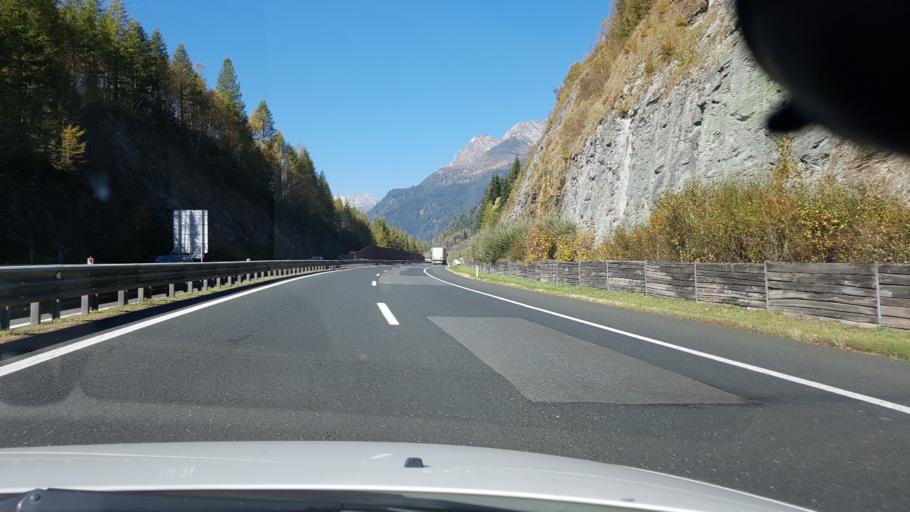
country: AT
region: Salzburg
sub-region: Politischer Bezirk Tamsweg
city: Zederhaus
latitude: 47.1426
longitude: 13.5247
